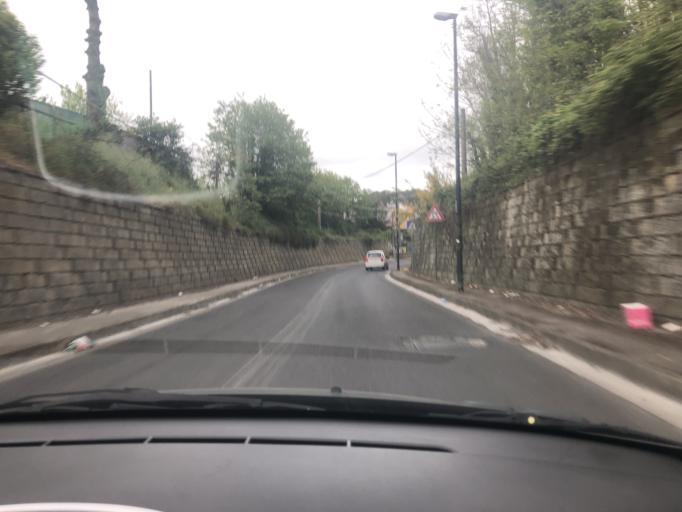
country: IT
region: Campania
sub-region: Provincia di Napoli
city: Torre Caracciolo
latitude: 40.8642
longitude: 14.1944
